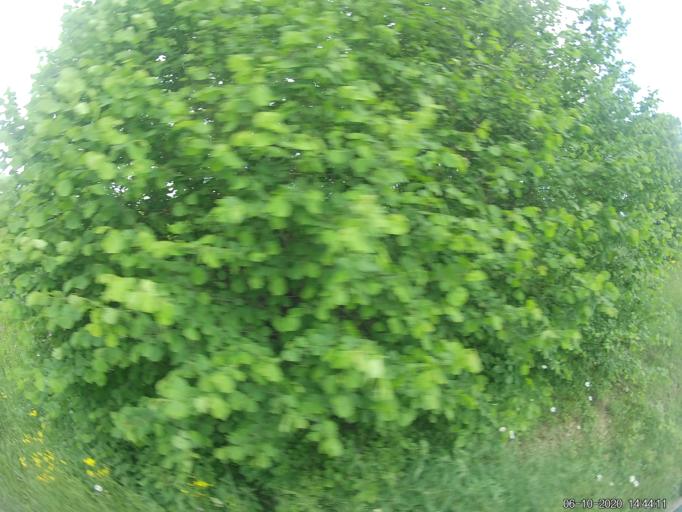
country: XK
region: Prizren
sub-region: Komuna e Therandes
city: Budakovo
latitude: 42.3818
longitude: 20.9445
